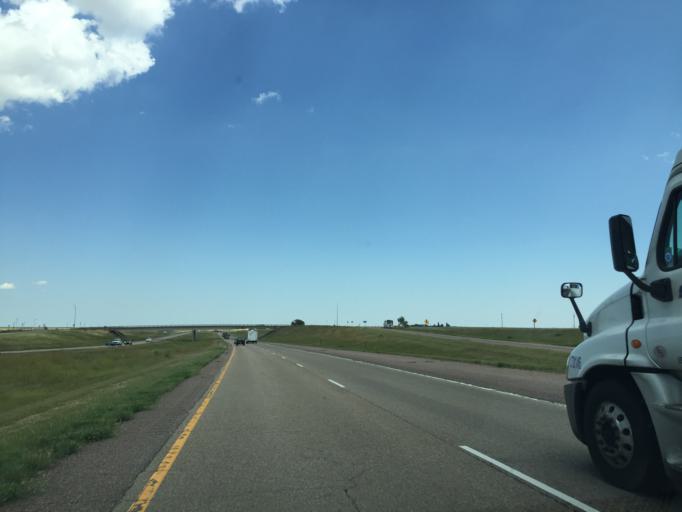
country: US
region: Colorado
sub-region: Lincoln County
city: Hugo
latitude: 39.2786
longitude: -103.4014
